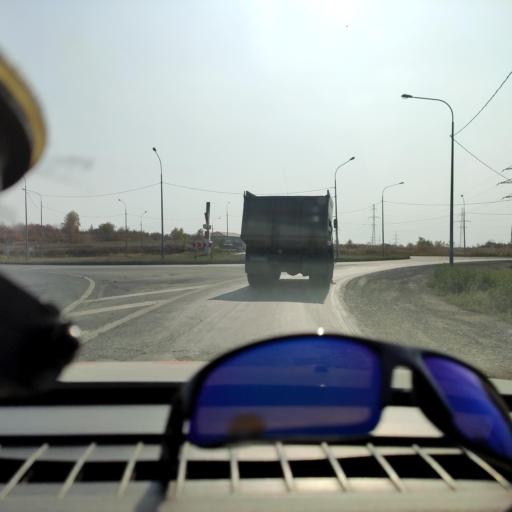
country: RU
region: Samara
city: Chapayevsk
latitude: 52.9980
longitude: 49.7681
